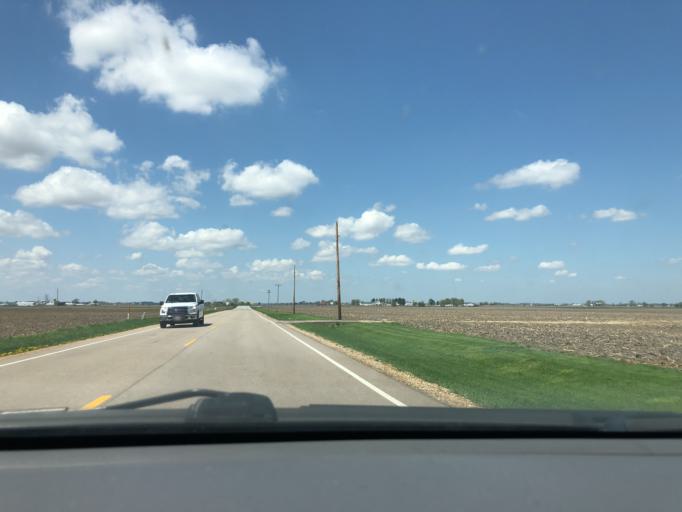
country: US
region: Illinois
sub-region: Kane County
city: Hampshire
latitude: 42.1064
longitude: -88.5462
